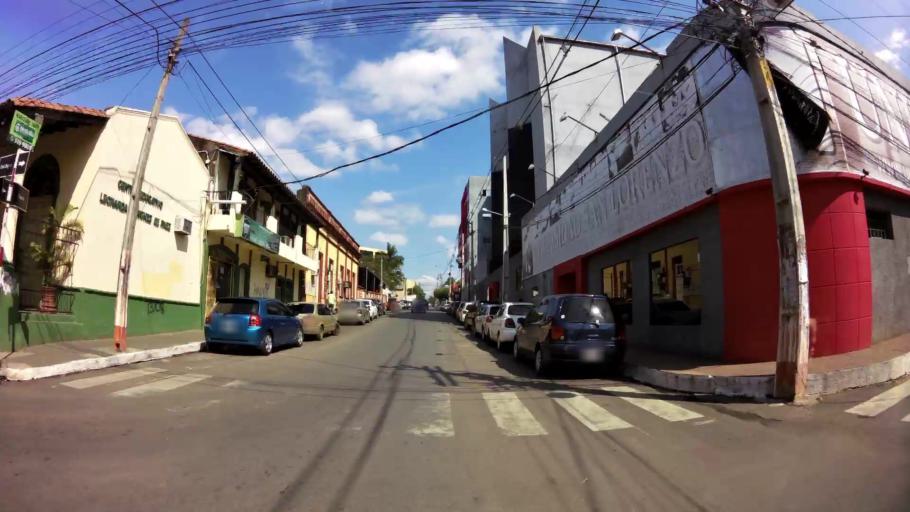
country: PY
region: Central
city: San Lorenzo
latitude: -25.3418
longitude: -57.5108
